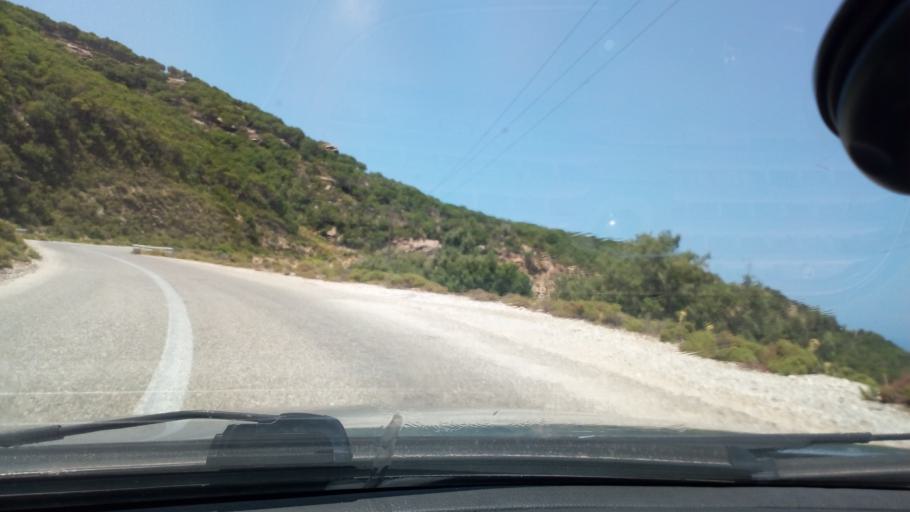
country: GR
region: North Aegean
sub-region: Nomos Samou
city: Agios Kirykos
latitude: 37.6377
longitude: 26.2557
